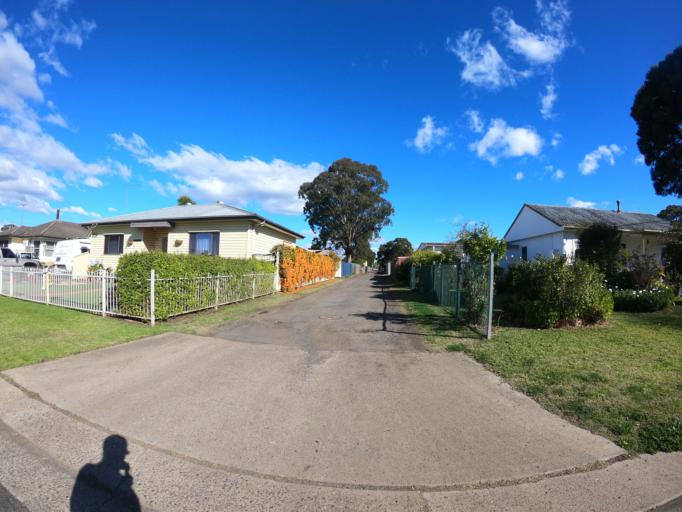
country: AU
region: New South Wales
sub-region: Hawkesbury
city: South Windsor
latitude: -33.6213
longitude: 150.8059
